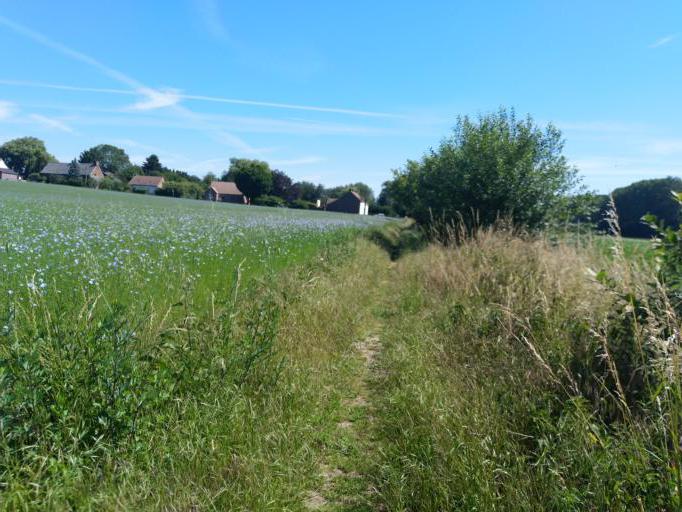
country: BE
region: Wallonia
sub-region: Province du Hainaut
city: Frameries
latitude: 50.3592
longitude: 3.8693
